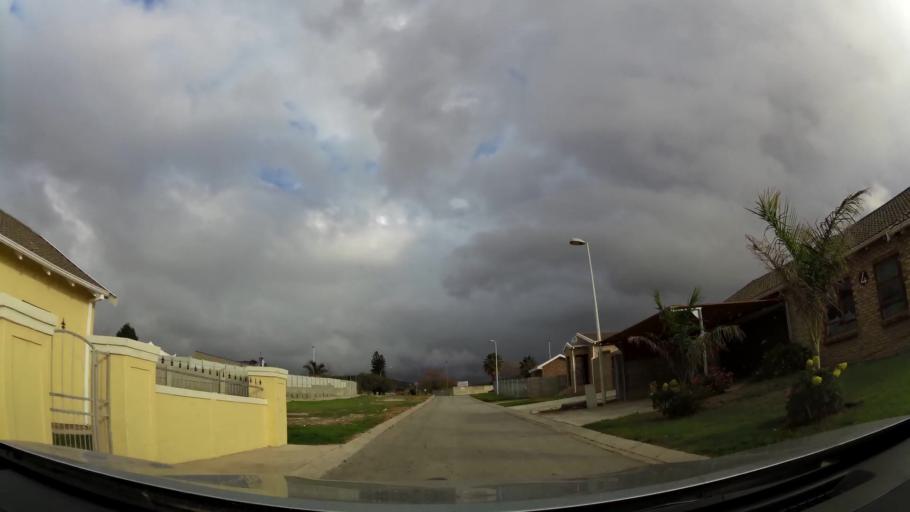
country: ZA
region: Eastern Cape
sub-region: Nelson Mandela Bay Metropolitan Municipality
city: Uitenhage
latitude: -33.7995
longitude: 25.4553
